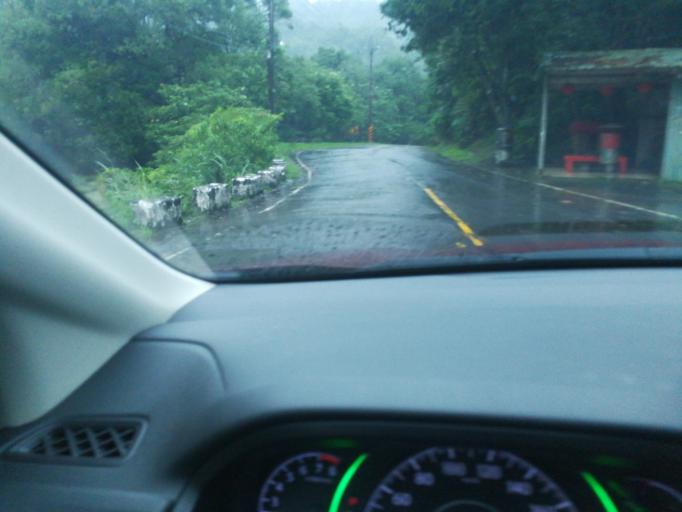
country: TW
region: Taipei
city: Taipei
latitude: 25.1098
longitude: 121.6252
